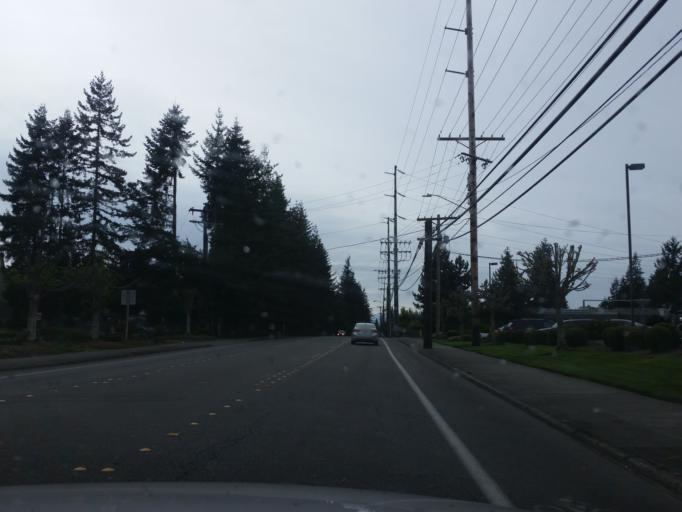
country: US
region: Washington
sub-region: Snohomish County
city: Lynnwood
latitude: 47.8284
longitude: -122.3102
